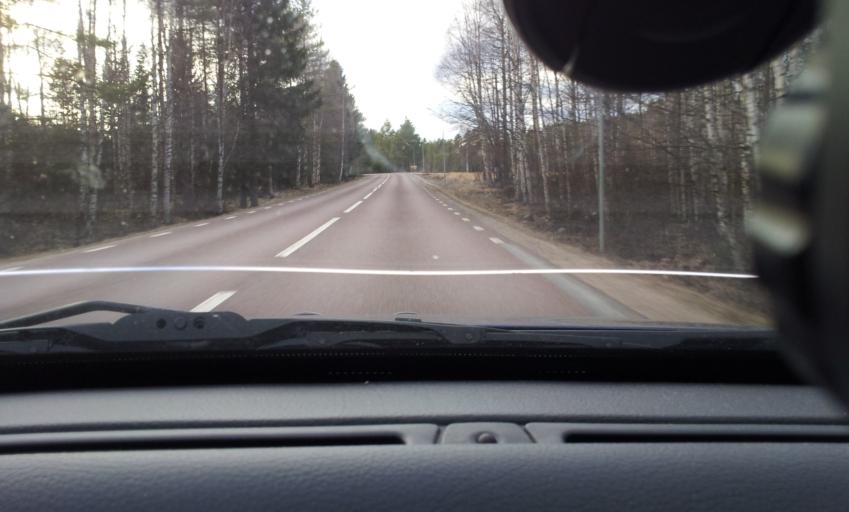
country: SE
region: Jaemtland
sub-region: Harjedalens Kommun
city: Sveg
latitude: 62.1768
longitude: 14.9126
